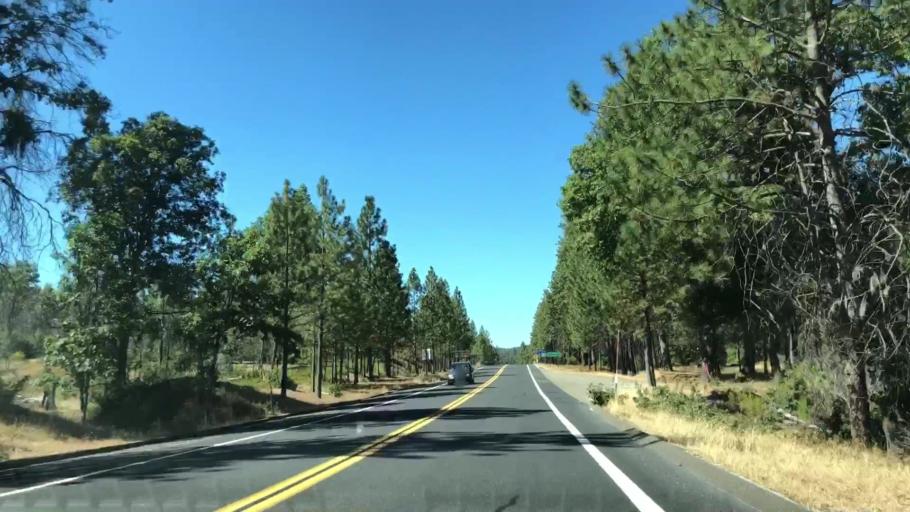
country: US
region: California
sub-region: Tuolumne County
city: Tuolumne City
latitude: 37.8187
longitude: -120.0538
